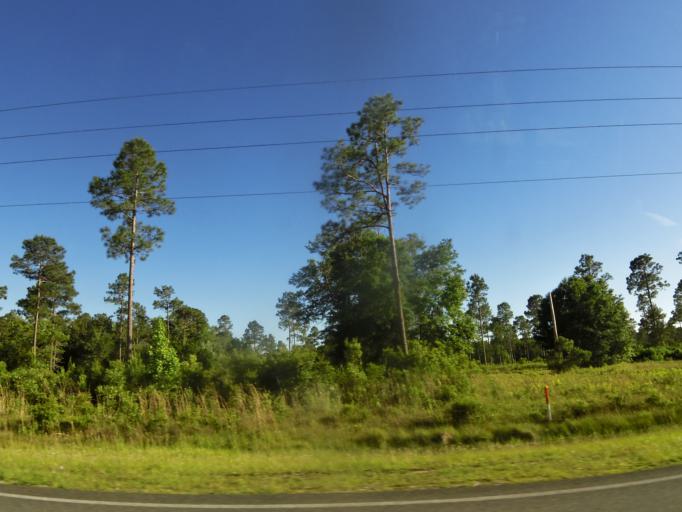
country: US
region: Florida
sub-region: Bradford County
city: Starke
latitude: 29.9275
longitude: -82.1089
